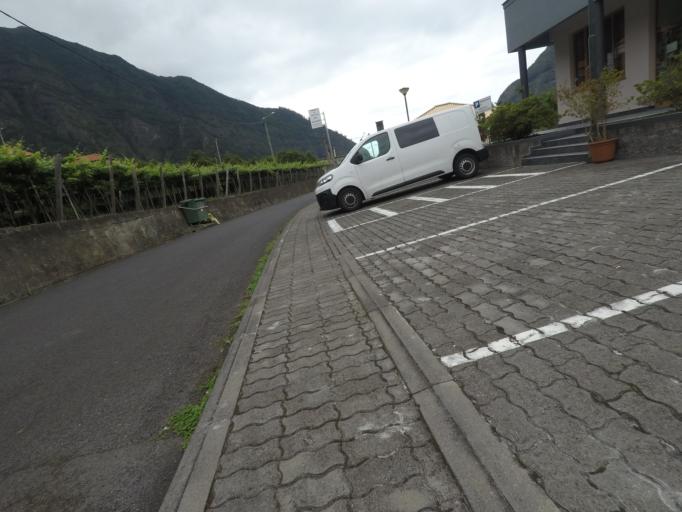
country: PT
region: Madeira
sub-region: Sao Vicente
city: Sao Vicente
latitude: 32.7914
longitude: -17.0394
